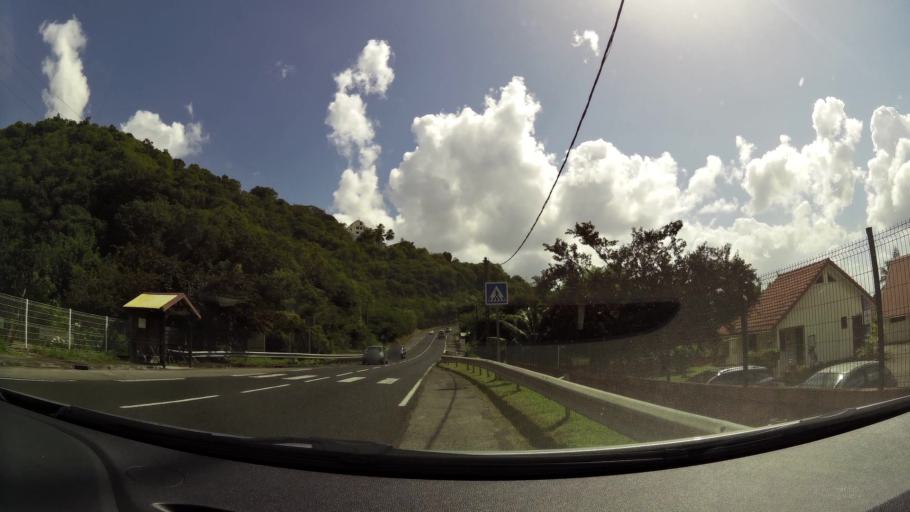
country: MQ
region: Martinique
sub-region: Martinique
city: Fort-de-France
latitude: 14.6365
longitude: -61.1303
